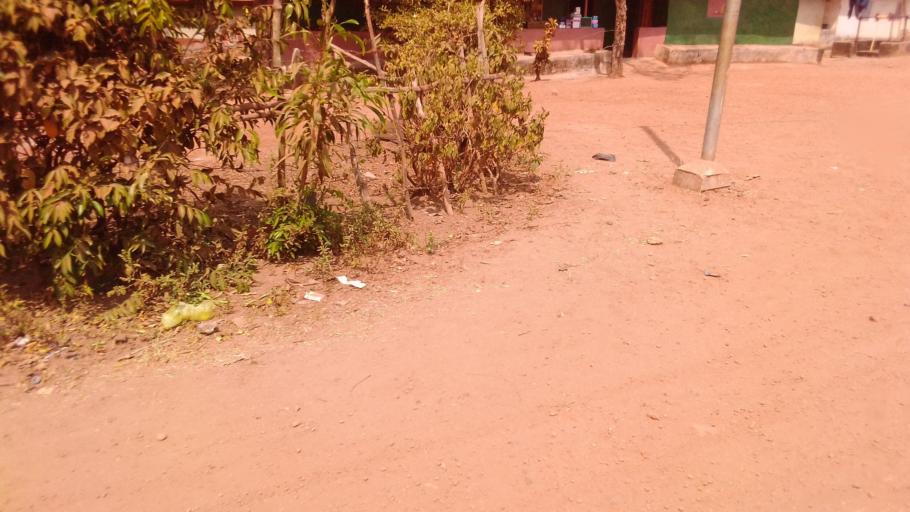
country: SL
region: Southern Province
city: Mogbwemo
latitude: 7.7968
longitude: -12.2977
